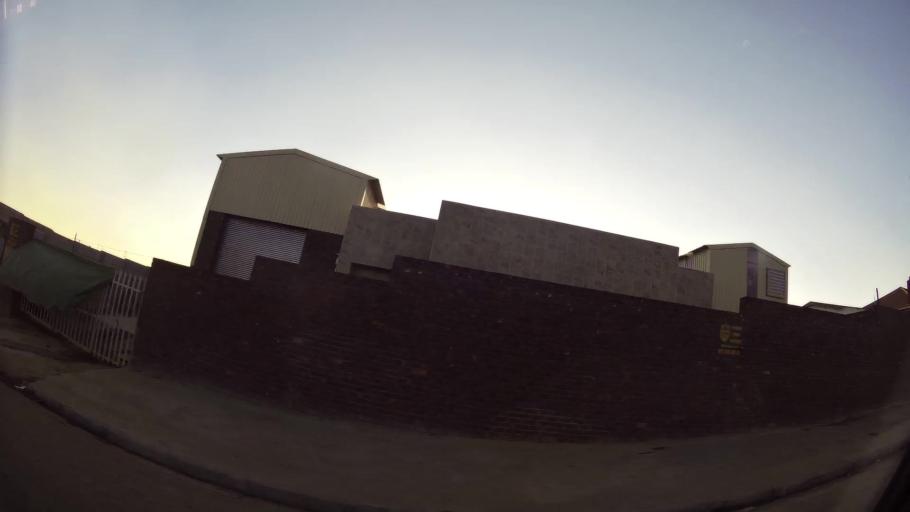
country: ZA
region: Gauteng
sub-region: Ekurhuleni Metropolitan Municipality
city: Germiston
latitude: -26.2533
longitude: 28.1320
